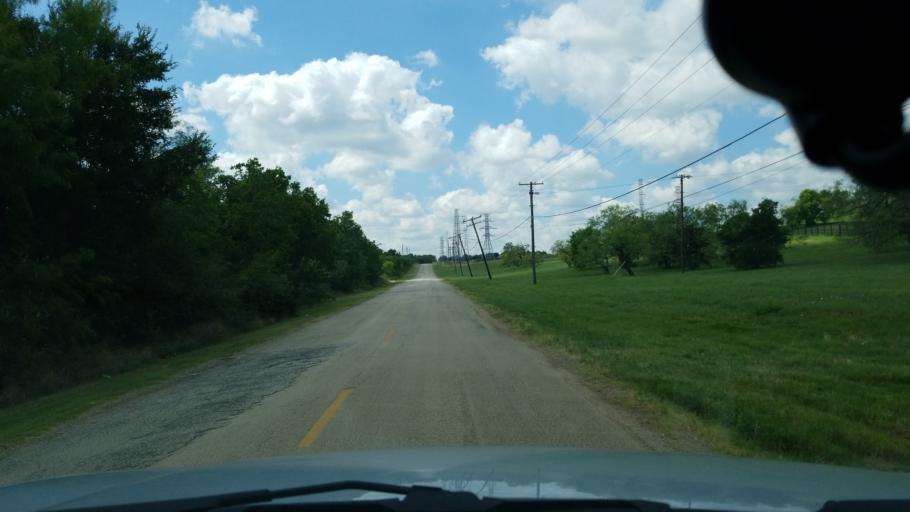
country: US
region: Texas
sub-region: Dallas County
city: Cockrell Hill
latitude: 32.7253
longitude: -96.9309
